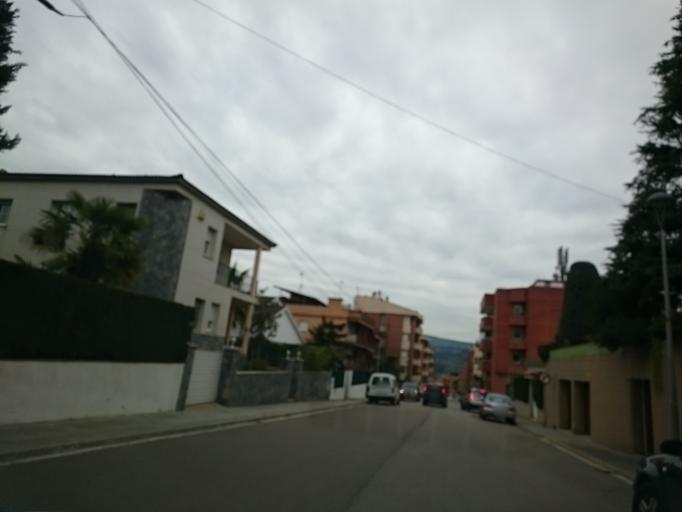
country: ES
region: Catalonia
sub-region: Provincia de Barcelona
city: Sant Sadurni d'Anoia
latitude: 41.4298
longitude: 1.7839
